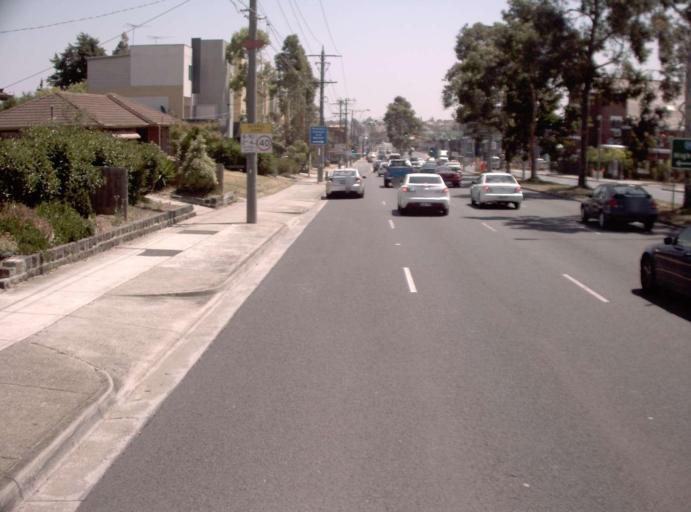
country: AU
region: Victoria
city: Thornbury
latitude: -37.7455
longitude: 145.0050
